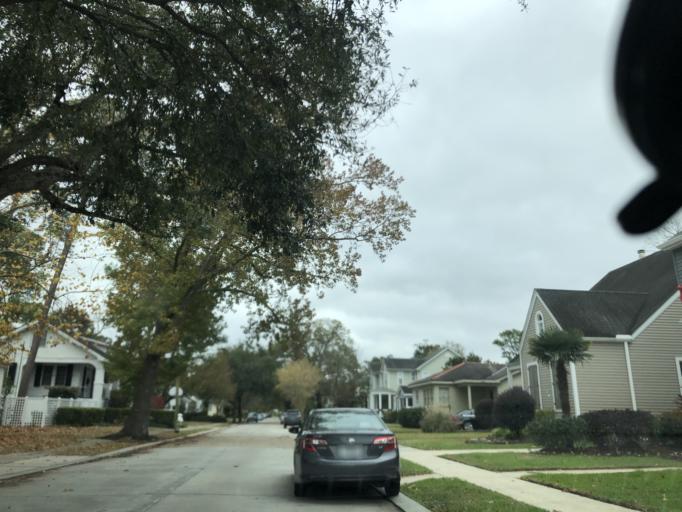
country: US
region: Louisiana
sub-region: Jefferson Parish
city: Metairie
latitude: 29.9802
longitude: -90.1501
